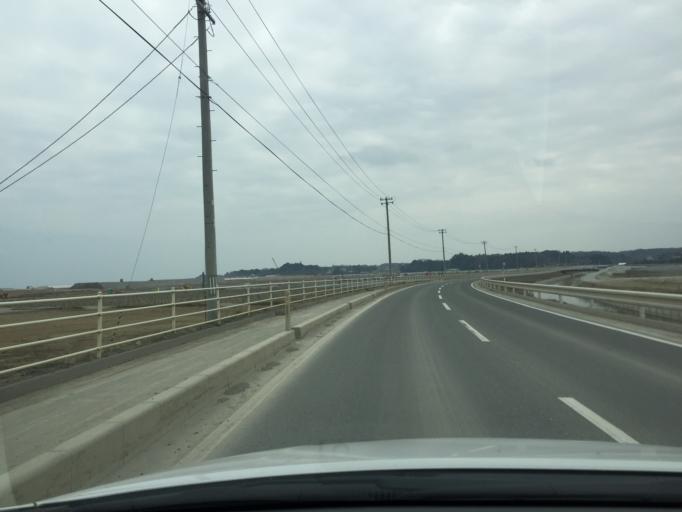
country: JP
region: Miyagi
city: Marumori
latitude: 37.7759
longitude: 140.9799
